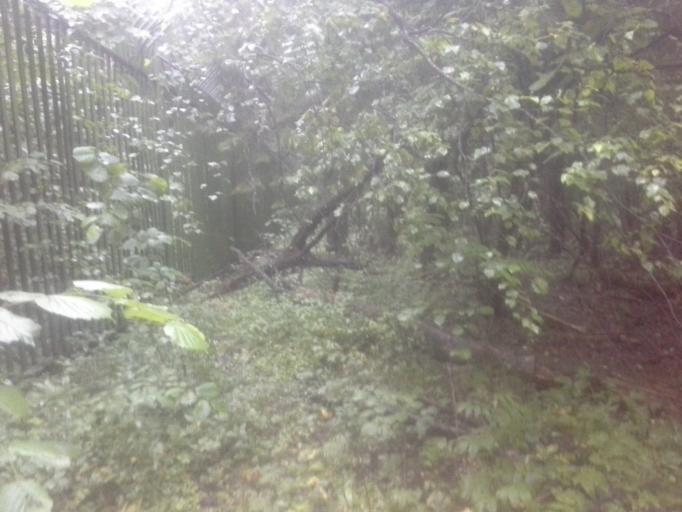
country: RU
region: Moskovskaya
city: Zhavoronki
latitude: 55.6687
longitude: 37.1136
